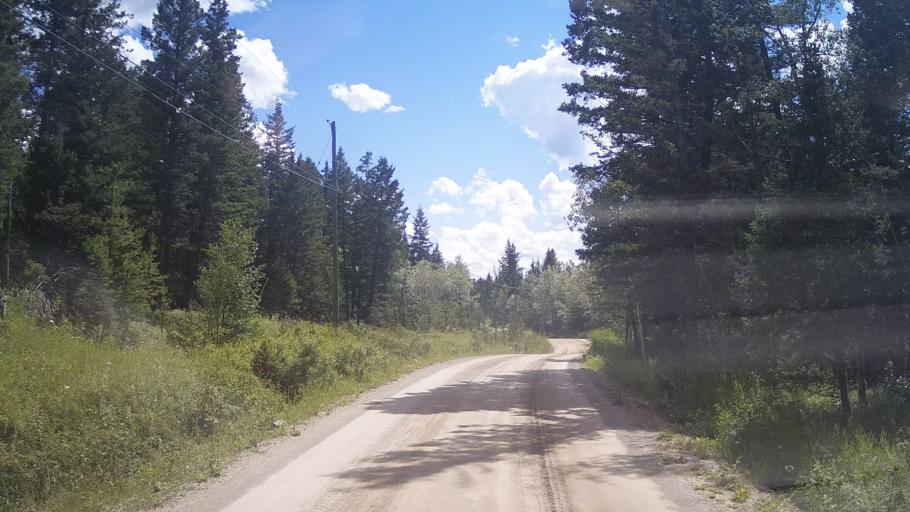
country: CA
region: British Columbia
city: Lillooet
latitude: 51.2842
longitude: -121.9673
